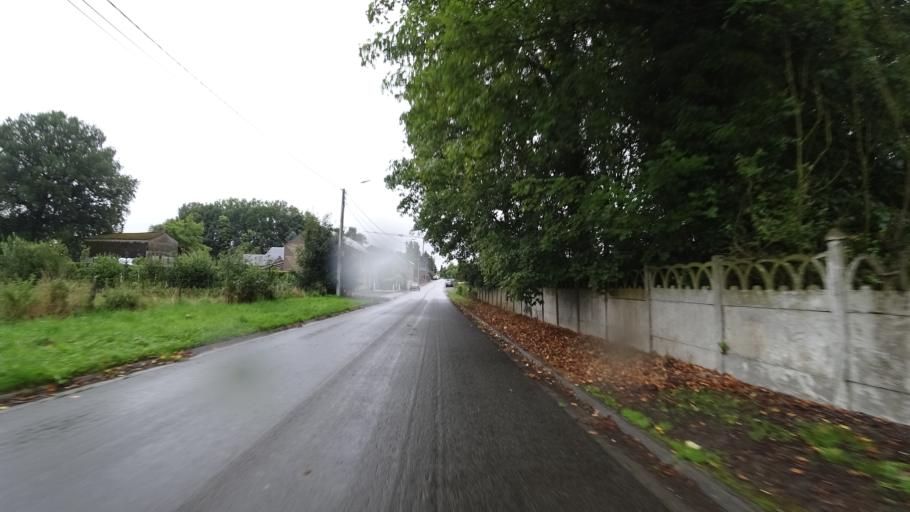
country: BE
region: Wallonia
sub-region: Province du Brabant Wallon
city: Perwez
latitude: 50.5317
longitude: 4.7902
